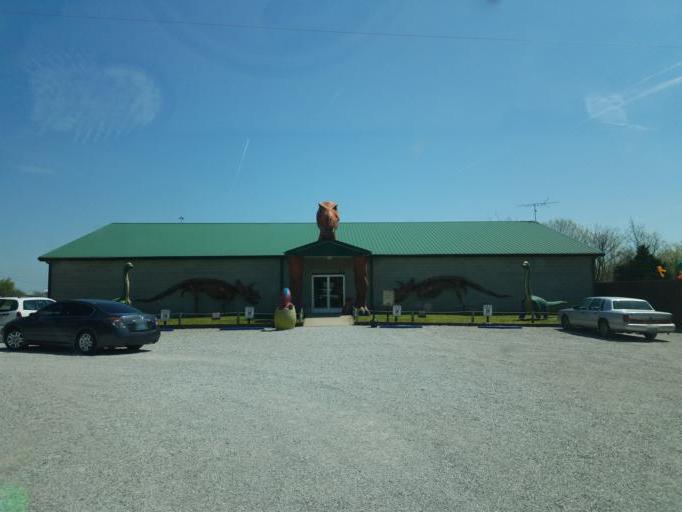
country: US
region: Kentucky
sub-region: Barren County
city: Cave City
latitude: 37.1356
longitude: -85.9815
